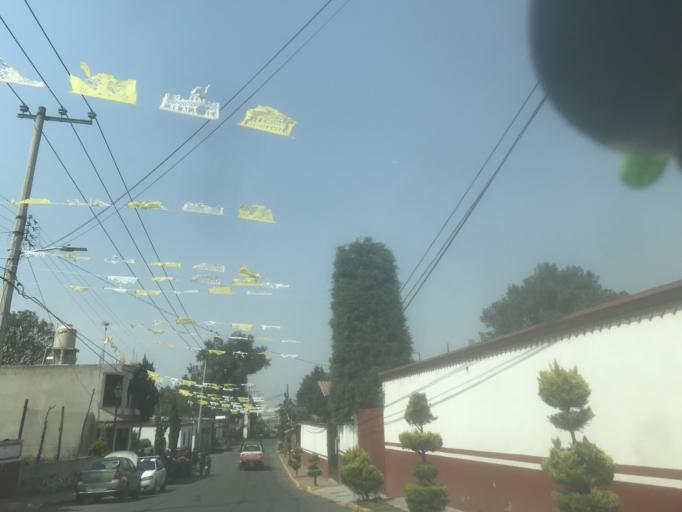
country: MX
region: Mexico
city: Ozumba de Alzate
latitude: 19.0290
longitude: -98.8011
